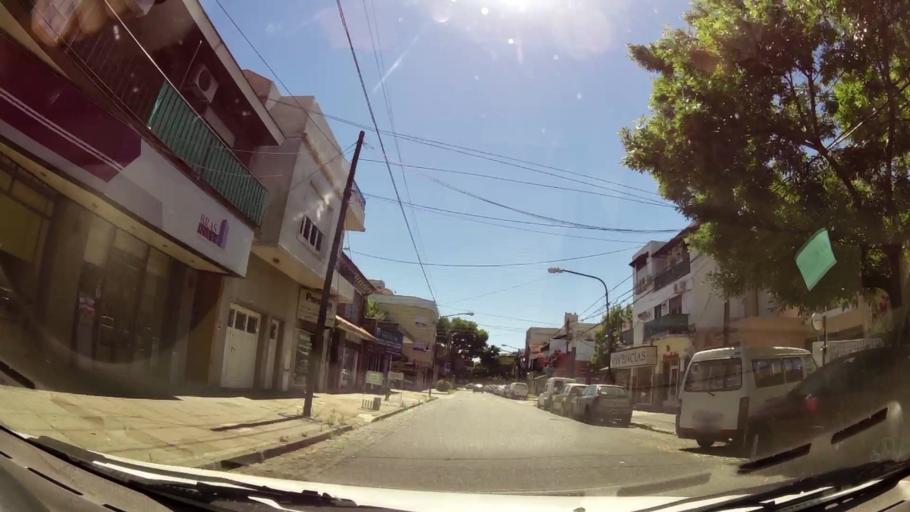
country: AR
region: Buenos Aires
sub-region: Partido de Vicente Lopez
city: Olivos
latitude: -34.5177
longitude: -58.4991
